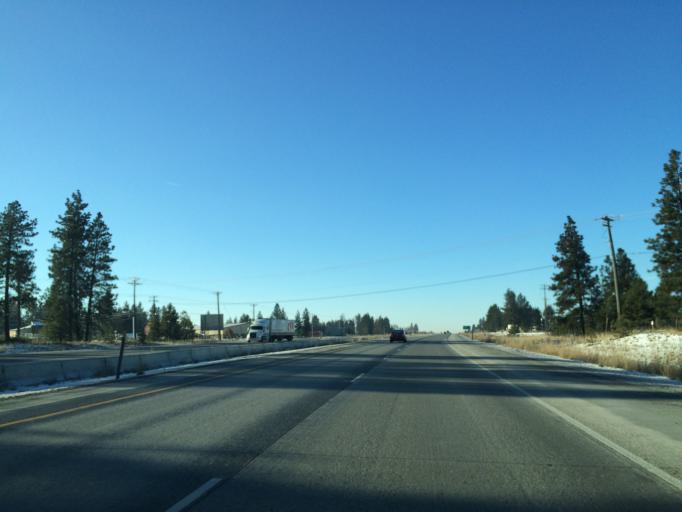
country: US
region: Washington
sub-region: Spokane County
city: Airway Heights
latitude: 47.6148
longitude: -117.5122
